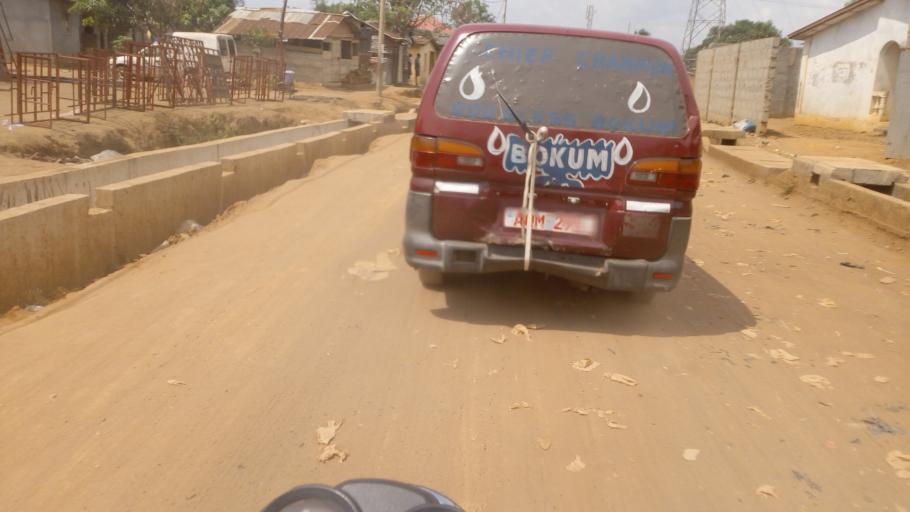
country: SL
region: Western Area
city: Waterloo
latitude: 8.3232
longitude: -13.0660
